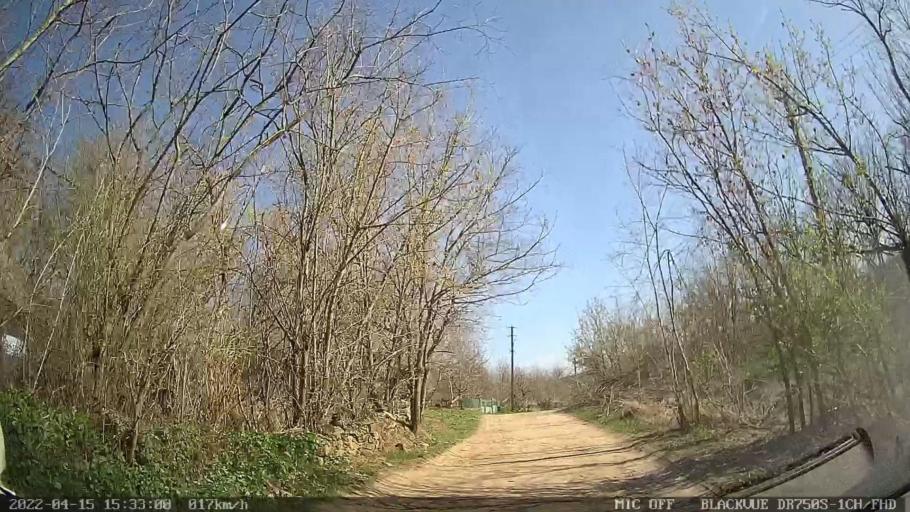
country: MD
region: Raionul Ocnita
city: Otaci
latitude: 48.3506
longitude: 27.9227
